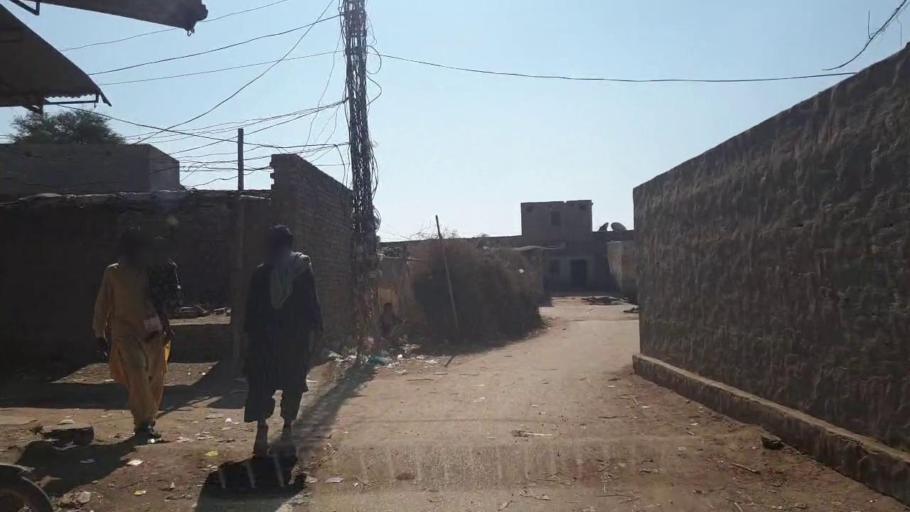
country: PK
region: Sindh
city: Shahpur Chakar
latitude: 26.1045
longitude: 68.6358
